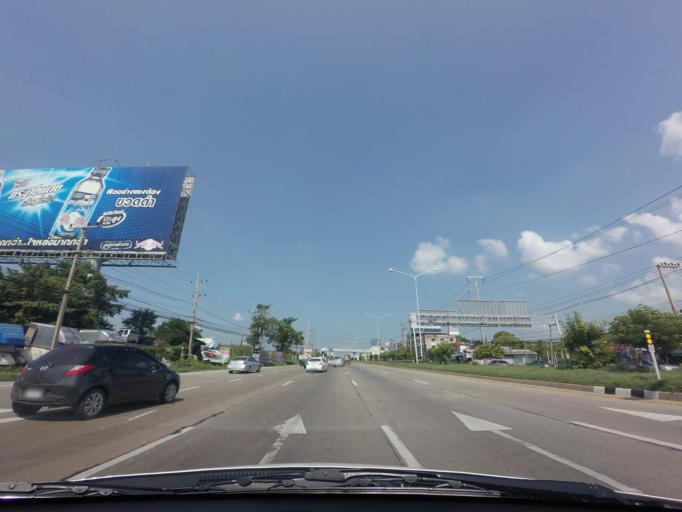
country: TH
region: Nakhon Pathom
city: Nakhon Chai Si
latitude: 13.7687
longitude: 100.1825
